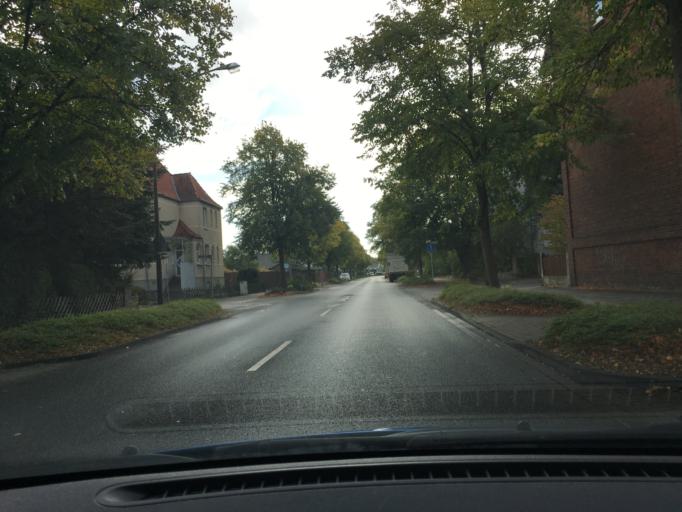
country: DE
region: Lower Saxony
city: Uelzen
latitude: 52.9695
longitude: 10.5726
